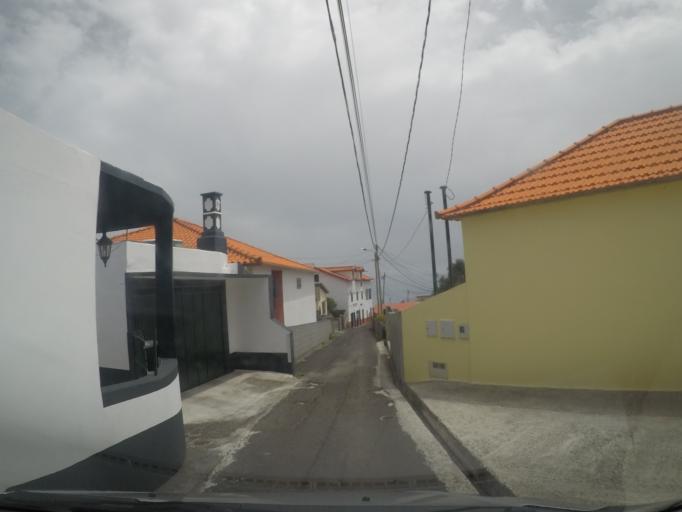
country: PT
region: Madeira
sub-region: Santa Cruz
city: Camacha
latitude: 32.6779
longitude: -16.8400
